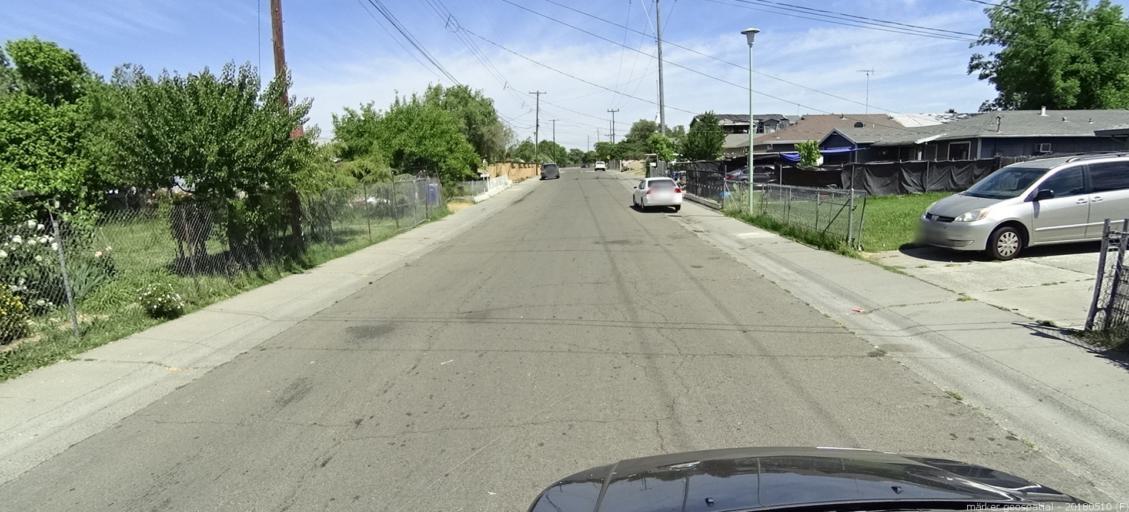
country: US
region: California
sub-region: Sacramento County
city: Rio Linda
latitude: 38.6385
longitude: -121.4497
